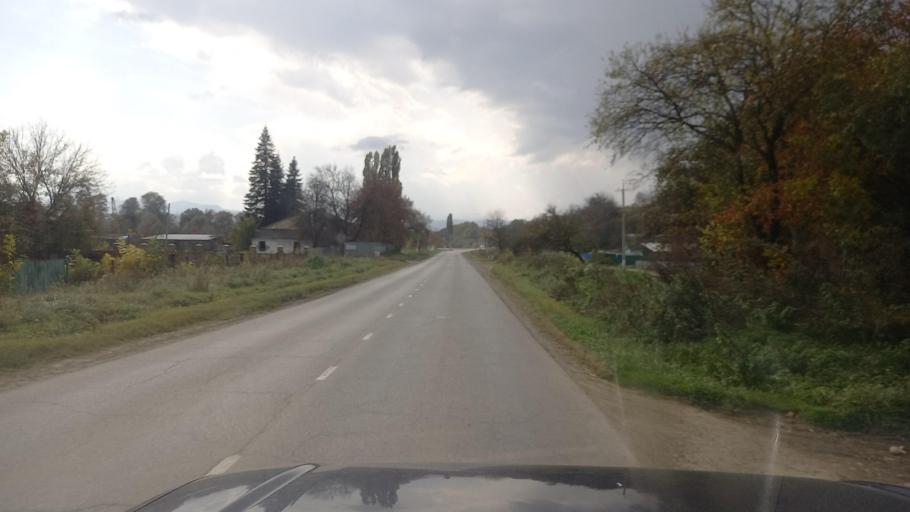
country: RU
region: Krasnodarskiy
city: Psebay
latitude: 44.1338
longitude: 40.8140
